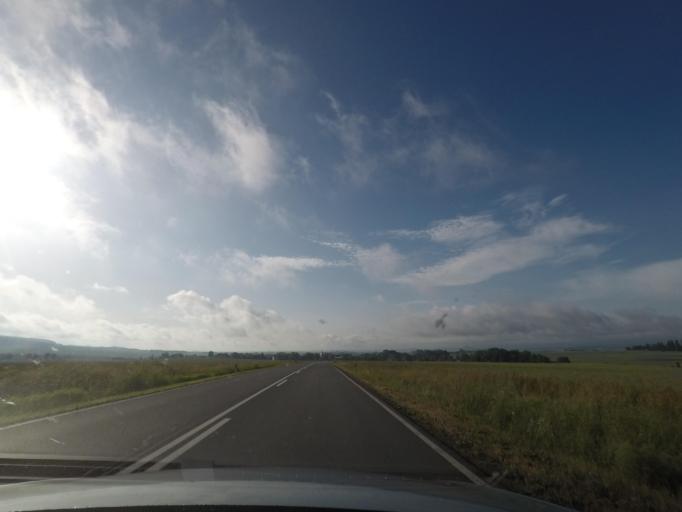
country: DE
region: Saxony-Anhalt
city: Huy-Neinstedt
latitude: 51.9430
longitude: 10.9000
